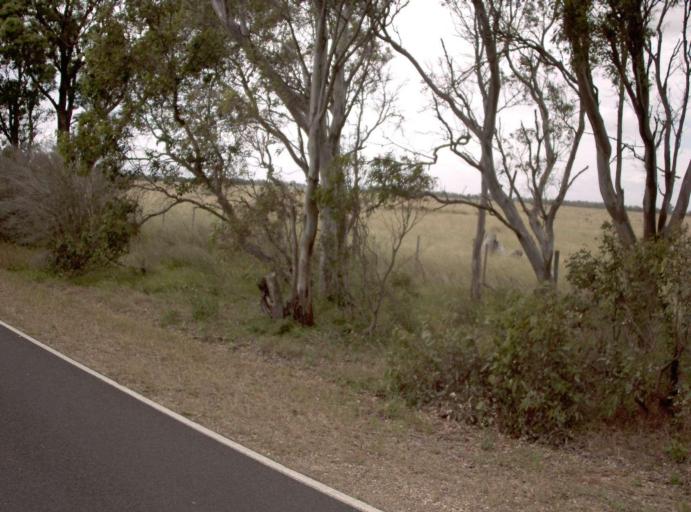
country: AU
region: Victoria
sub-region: Wellington
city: Sale
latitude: -37.9658
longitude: 147.1330
